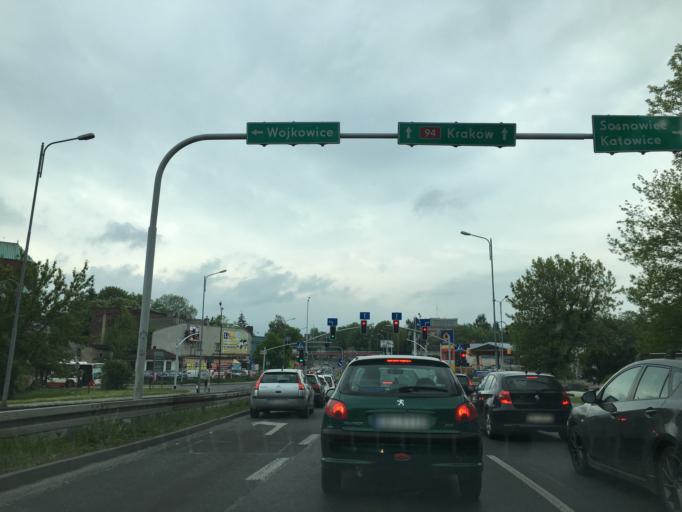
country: PL
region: Silesian Voivodeship
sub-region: Powiat bedzinski
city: Czeladz
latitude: 50.3174
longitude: 19.0692
